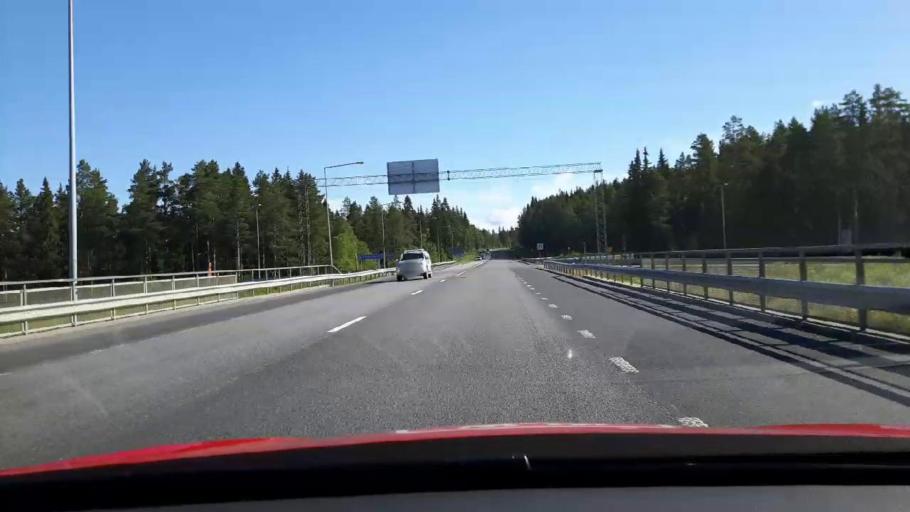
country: SE
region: Jaemtland
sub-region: OEstersunds Kommun
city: Ostersund
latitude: 63.2028
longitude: 14.6774
